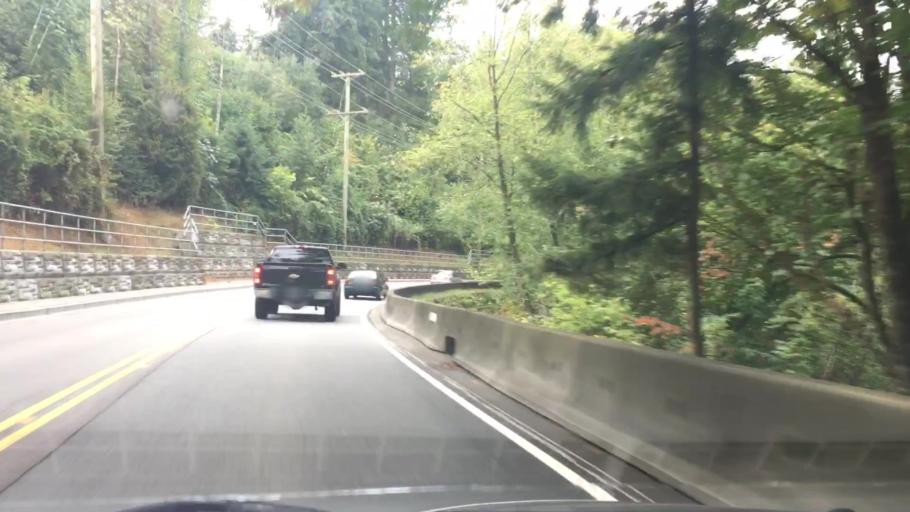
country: CA
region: British Columbia
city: Langley
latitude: 49.1046
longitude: -122.5680
